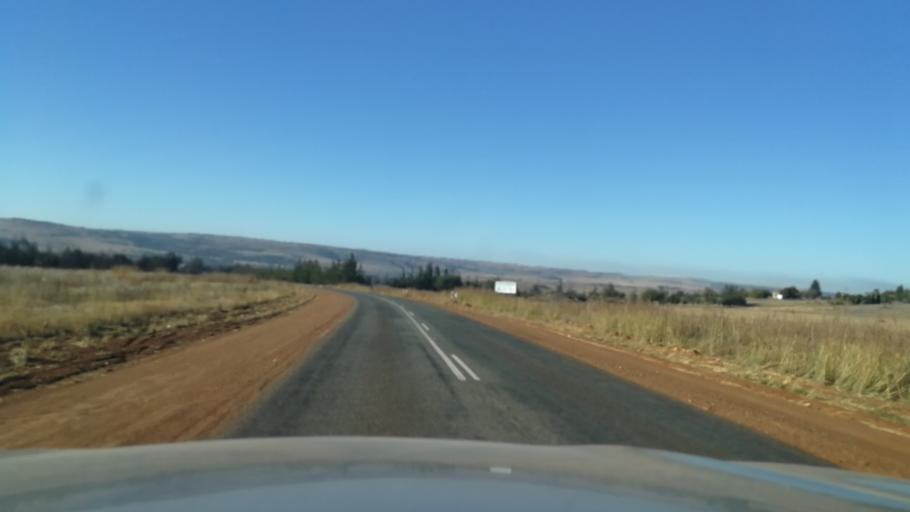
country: ZA
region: Gauteng
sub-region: West Rand District Municipality
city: Krugersdorp
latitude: -26.0000
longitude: 27.7017
